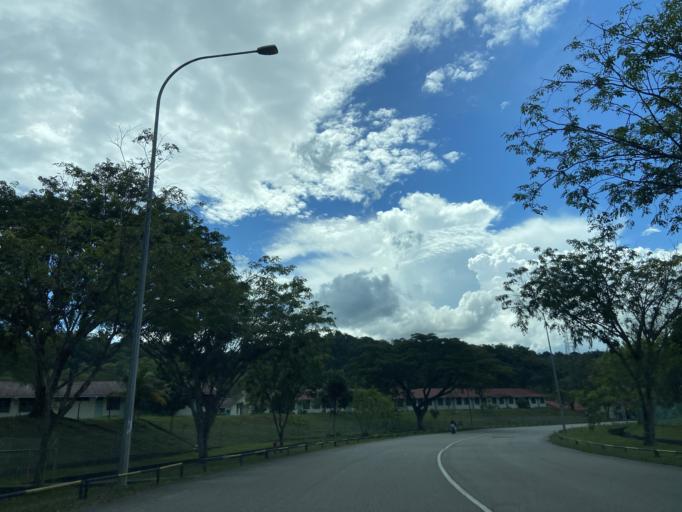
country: SG
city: Singapore
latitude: 1.0568
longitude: 104.0268
